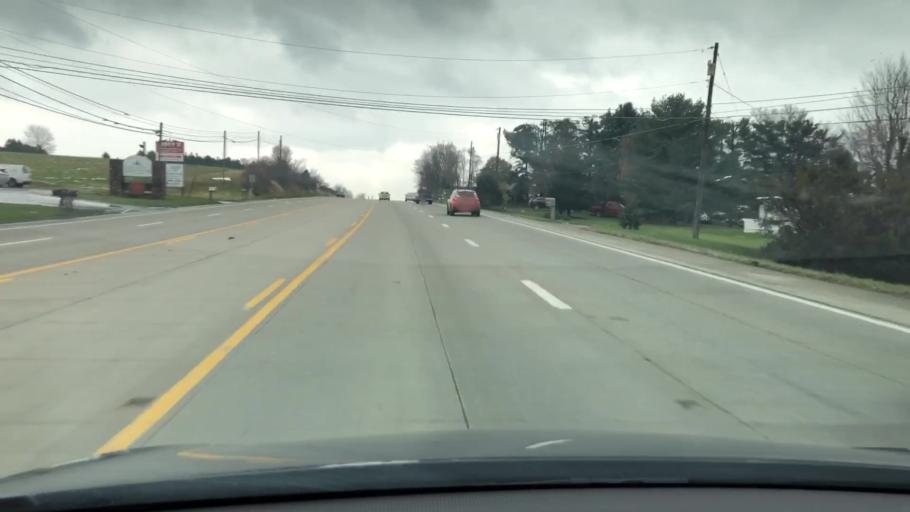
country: US
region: Pennsylvania
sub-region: Fayette County
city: Dunbar
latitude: 39.9567
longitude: -79.6511
